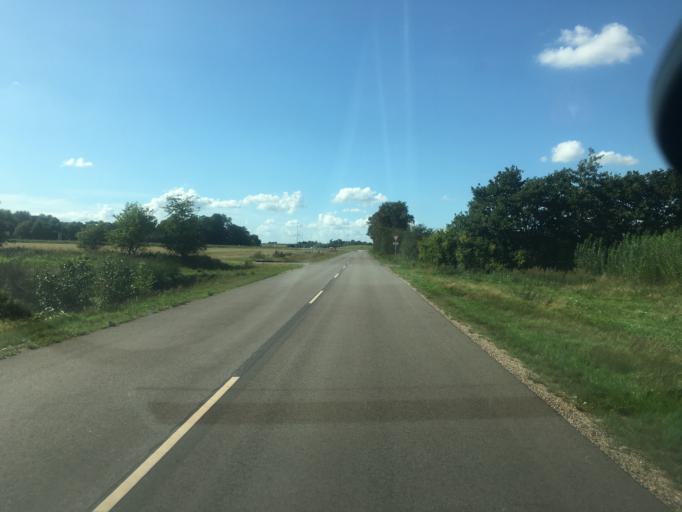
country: DE
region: Schleswig-Holstein
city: Ellhoft
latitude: 54.9680
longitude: 8.9706
